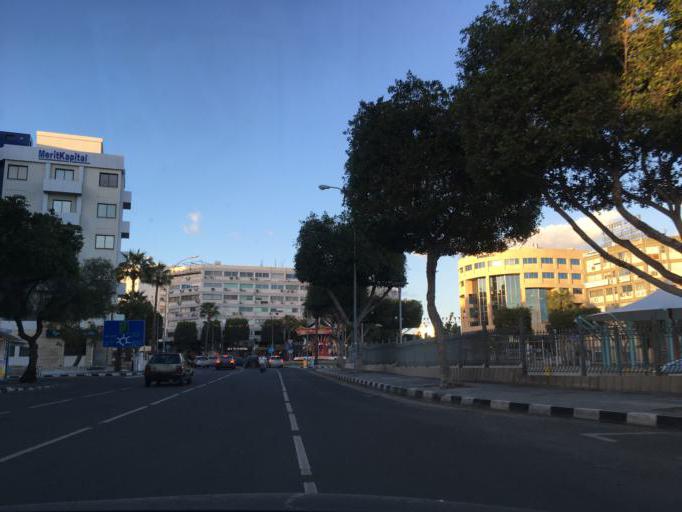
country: CY
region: Limassol
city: Limassol
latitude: 34.6858
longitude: 33.0533
